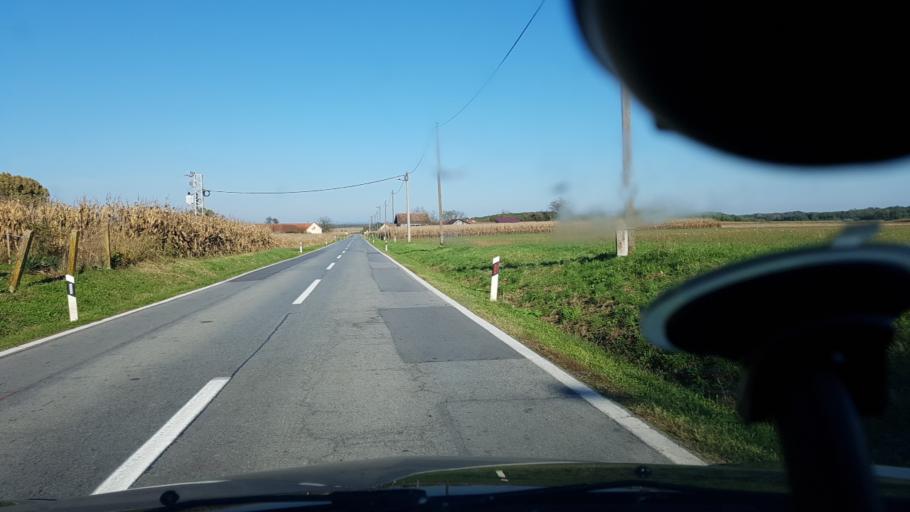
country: HR
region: Bjelovarsko-Bilogorska
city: Gudovac
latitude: 45.8229
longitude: 16.7387
